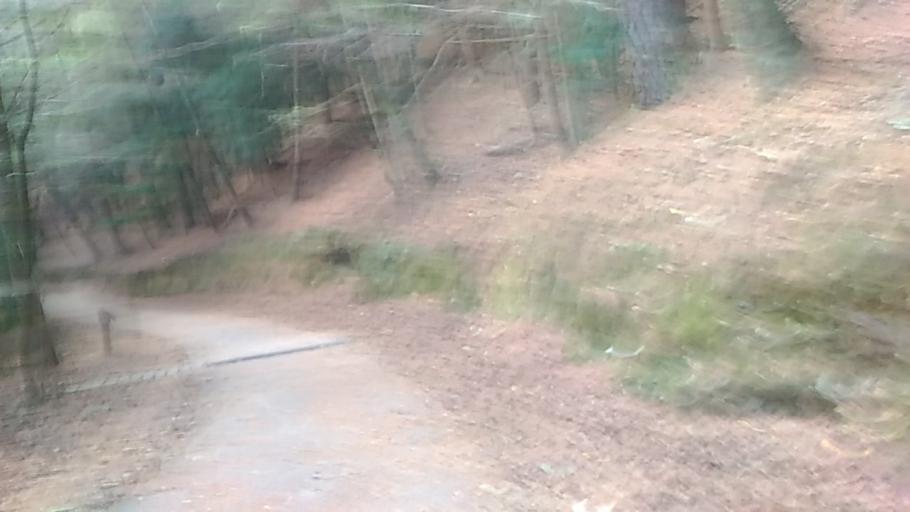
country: TW
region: Taiwan
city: Daxi
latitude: 24.4062
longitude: 121.3047
